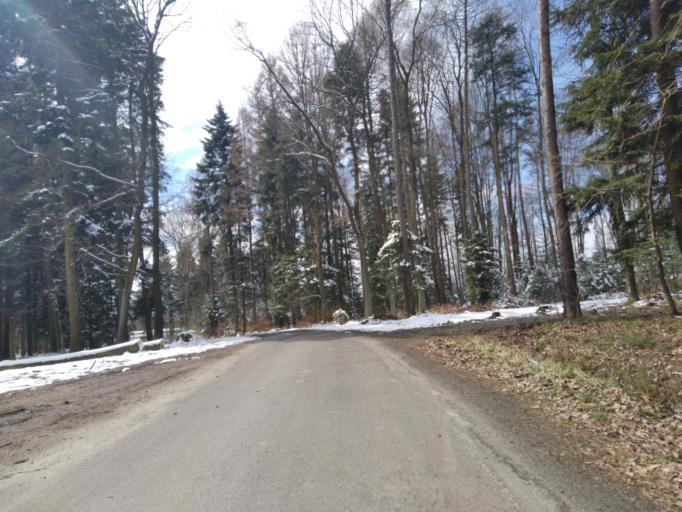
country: PL
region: Subcarpathian Voivodeship
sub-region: Powiat ropczycko-sedziszowski
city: Ropczyce
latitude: 50.0139
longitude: 21.5977
